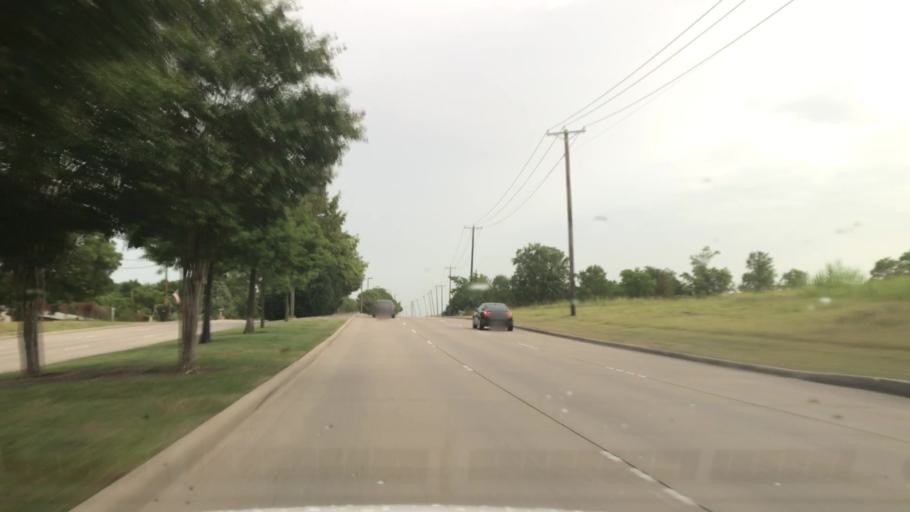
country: US
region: Texas
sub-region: Dallas County
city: Mesquite
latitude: 32.7286
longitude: -96.5519
